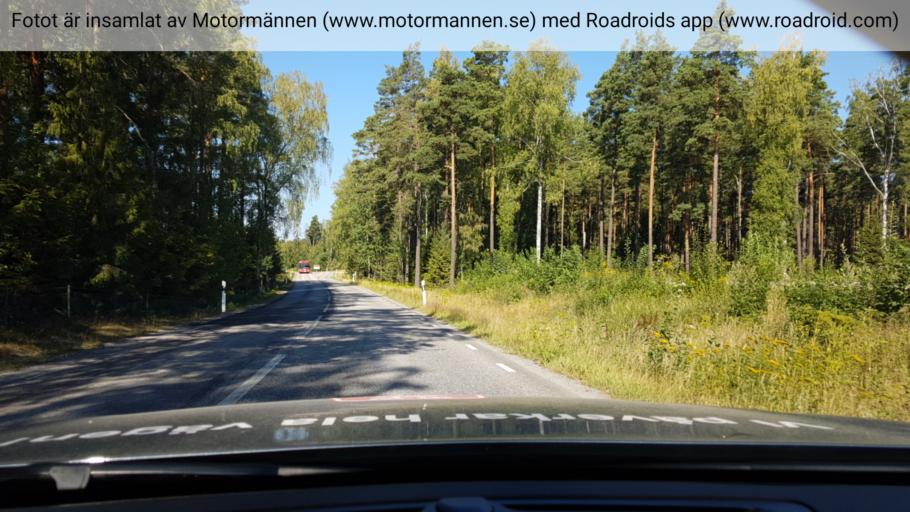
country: SE
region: Stockholm
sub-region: Ekero Kommun
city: Ekeroe
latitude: 59.2808
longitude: 17.7519
